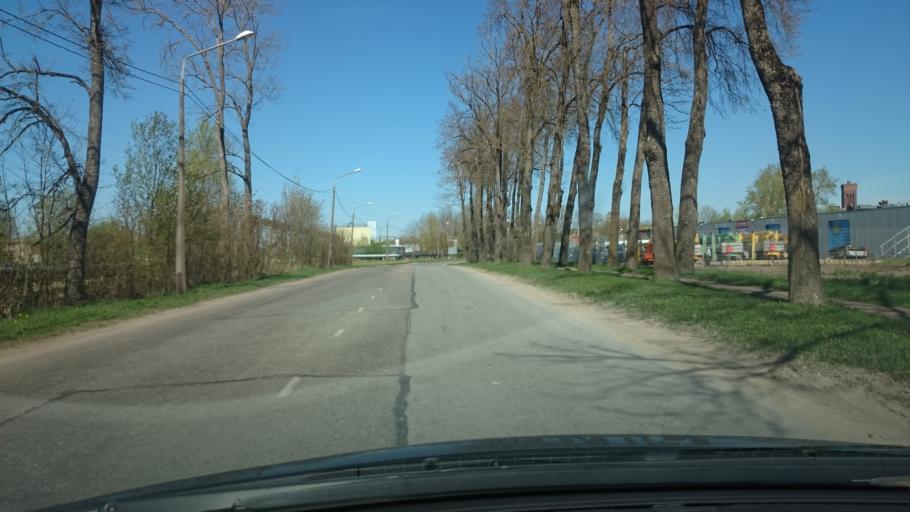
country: EE
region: Ida-Virumaa
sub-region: Narva linn
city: Narva
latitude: 59.3558
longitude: 28.1831
